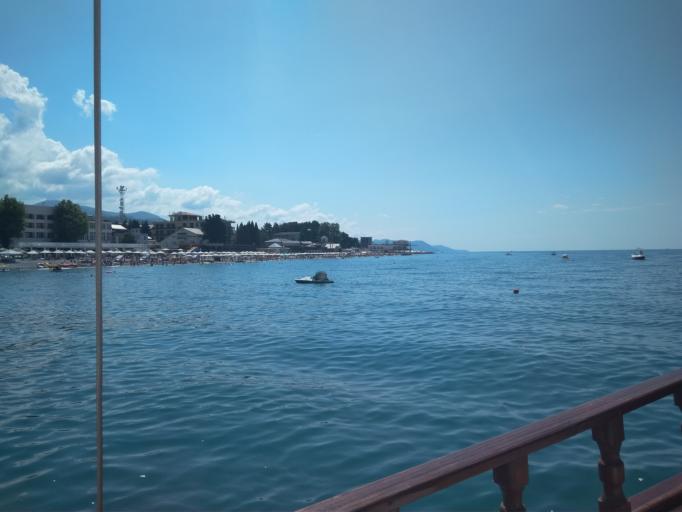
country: RU
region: Krasnodarskiy
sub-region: Sochi City
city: Lazarevskoye
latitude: 43.9044
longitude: 39.3254
